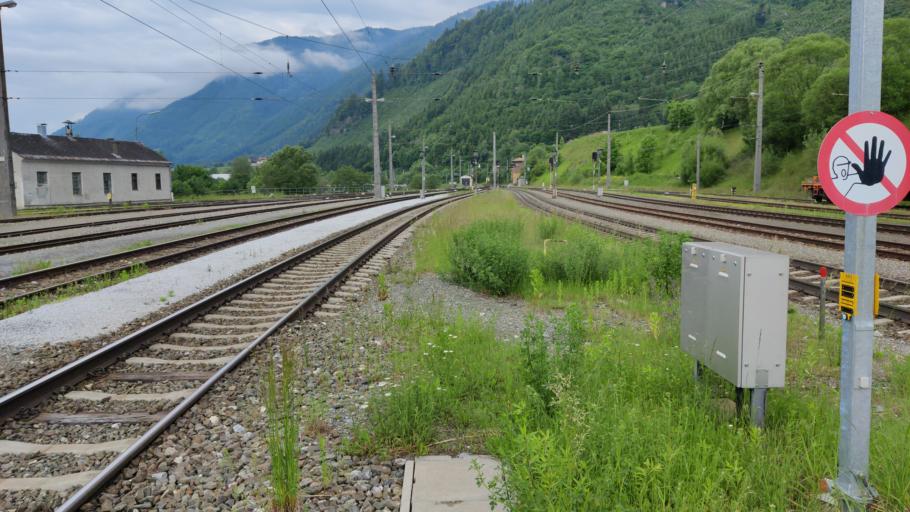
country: AT
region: Styria
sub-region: Politischer Bezirk Murtal
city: Sankt Georgen ob Judenburg
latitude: 47.2005
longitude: 14.4410
